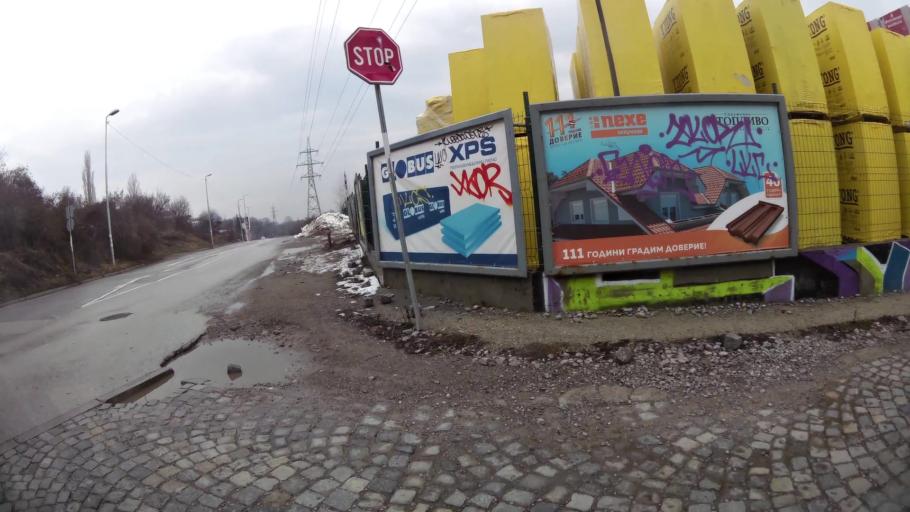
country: BG
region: Sofia-Capital
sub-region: Stolichna Obshtina
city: Sofia
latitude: 42.6714
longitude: 23.2418
